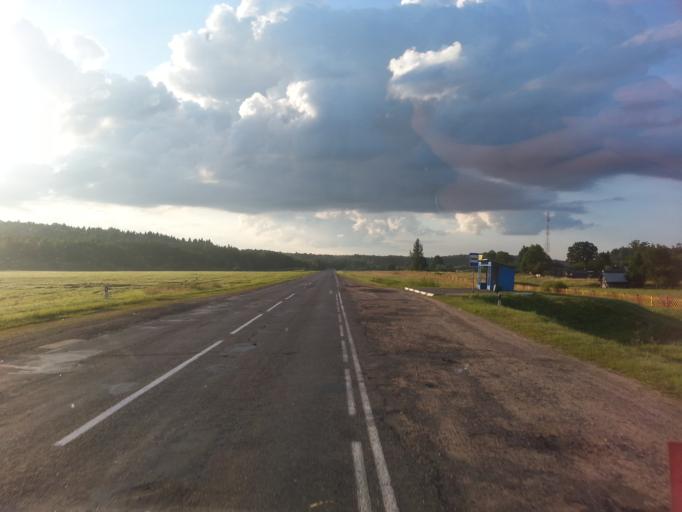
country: BY
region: Minsk
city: Il'ya
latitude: 54.4770
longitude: 27.2582
